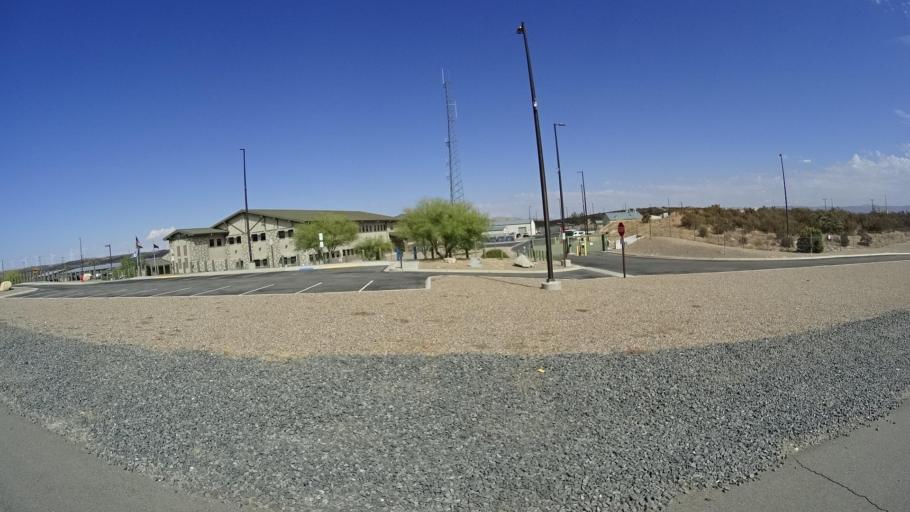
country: US
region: California
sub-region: San Diego County
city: Campo
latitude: 32.6819
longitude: -116.2929
